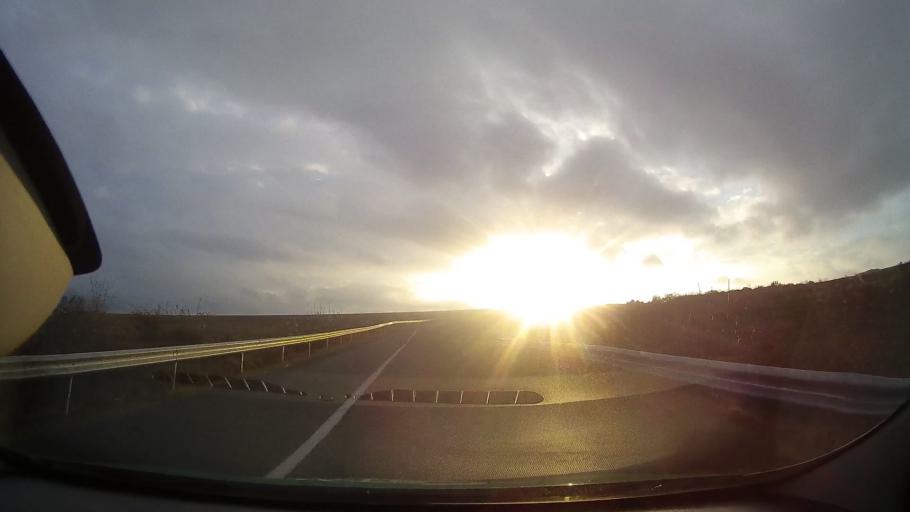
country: RO
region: Constanta
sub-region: Comuna Adamclisi
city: Adamclisi
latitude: 44.0359
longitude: 27.9382
